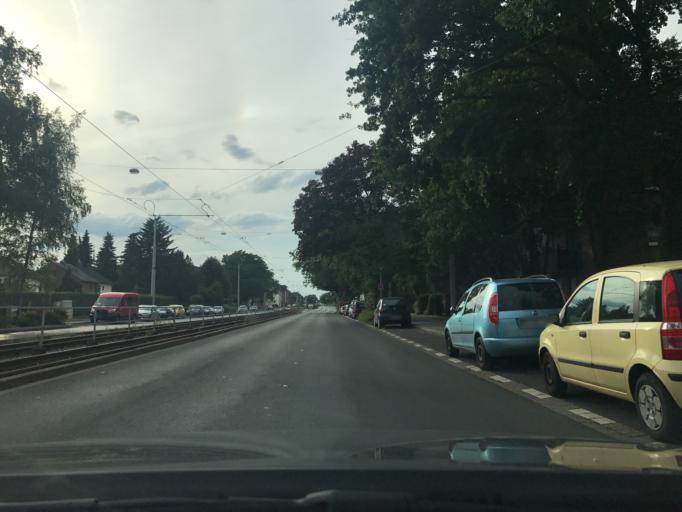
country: DE
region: North Rhine-Westphalia
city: Tonisvorst
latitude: 51.3555
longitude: 6.5319
